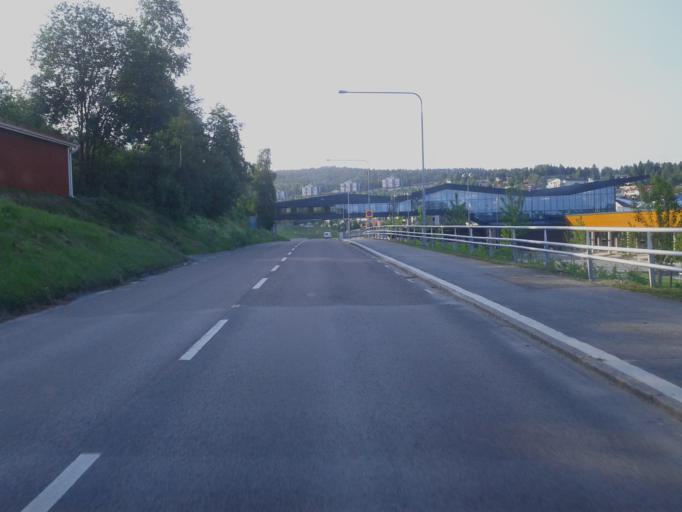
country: SE
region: Vaesternorrland
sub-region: OErnskoeldsviks Kommun
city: Ornskoldsvik
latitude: 63.2863
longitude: 18.7074
